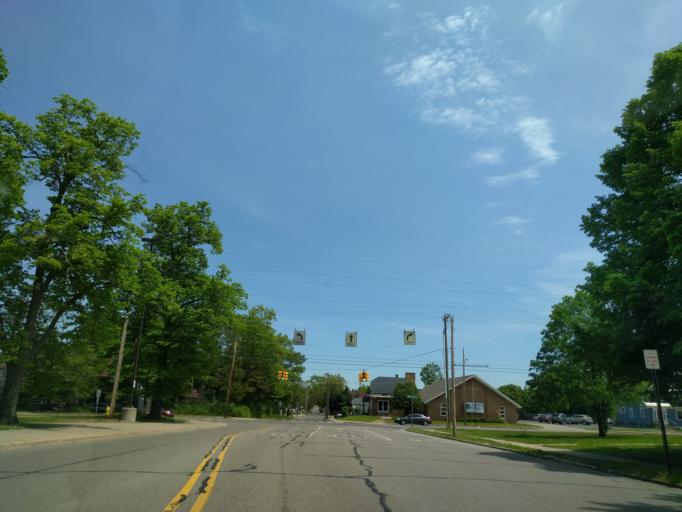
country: US
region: Michigan
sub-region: Marquette County
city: Marquette
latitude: 46.5556
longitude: -87.3972
